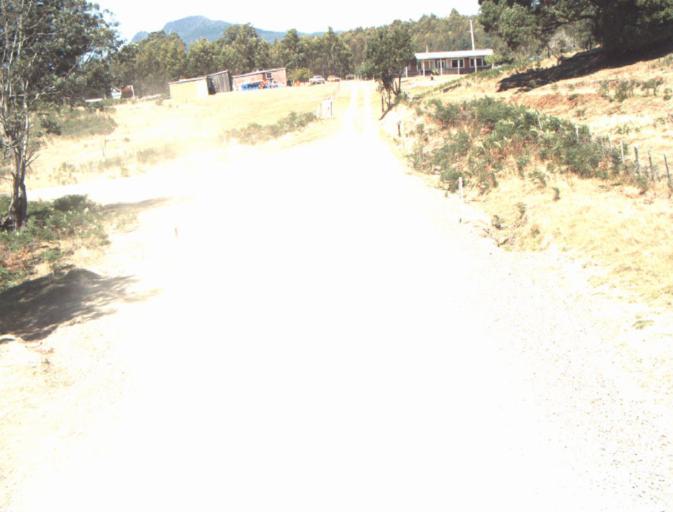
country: AU
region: Tasmania
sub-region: Dorset
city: Scottsdale
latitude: -41.2974
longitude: 147.3559
